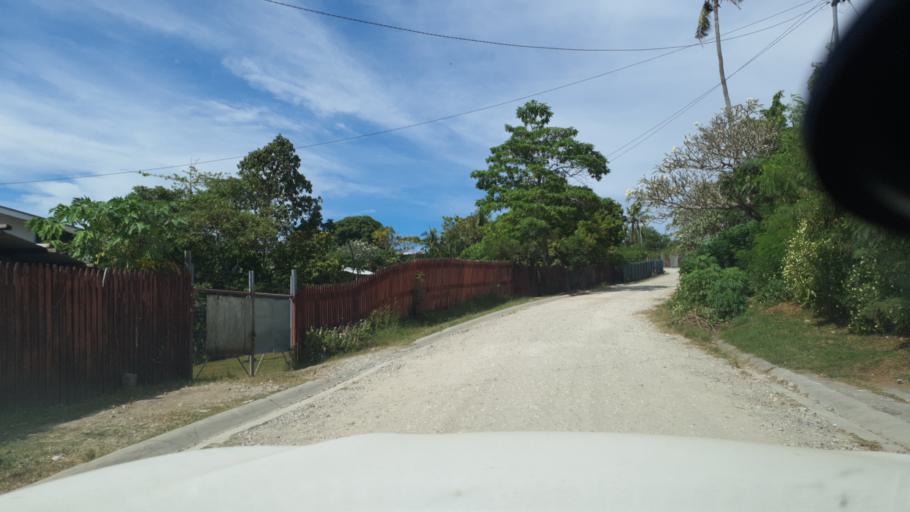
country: SB
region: Guadalcanal
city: Honiara
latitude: -9.4409
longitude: 159.9734
